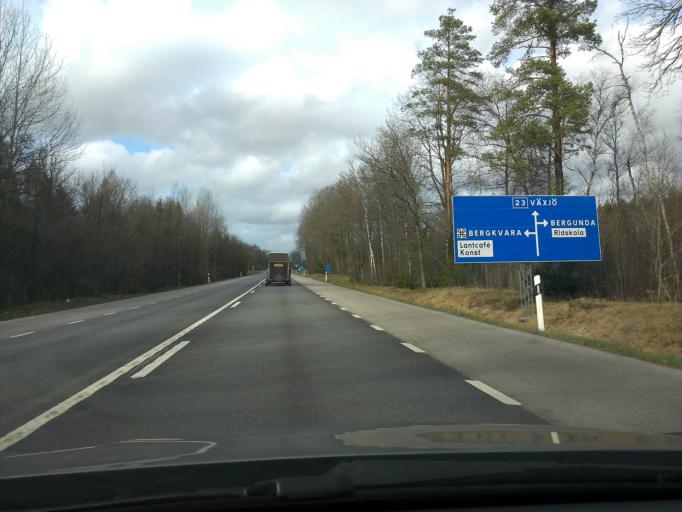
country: SE
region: Kronoberg
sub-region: Vaxjo Kommun
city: Vaexjoe
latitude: 56.8634
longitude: 14.7338
